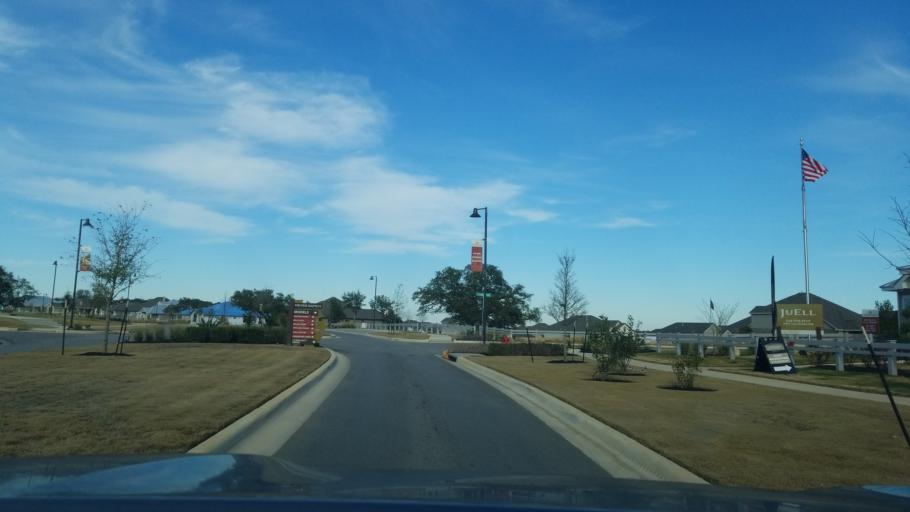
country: US
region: Texas
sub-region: Comal County
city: Canyon Lake
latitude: 29.7770
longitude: -98.2877
